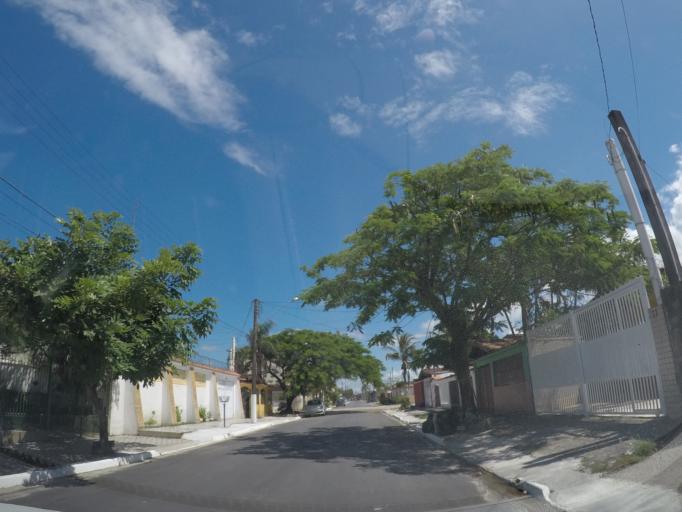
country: BR
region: Sao Paulo
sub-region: Mongagua
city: Mongagua
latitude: -24.0631
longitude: -46.5577
